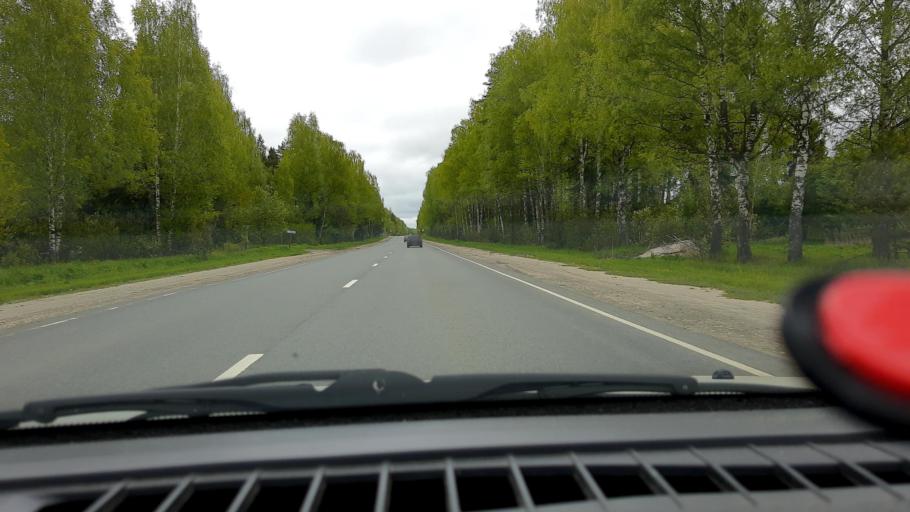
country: RU
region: Nizjnij Novgorod
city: Linda
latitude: 56.6235
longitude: 44.0787
